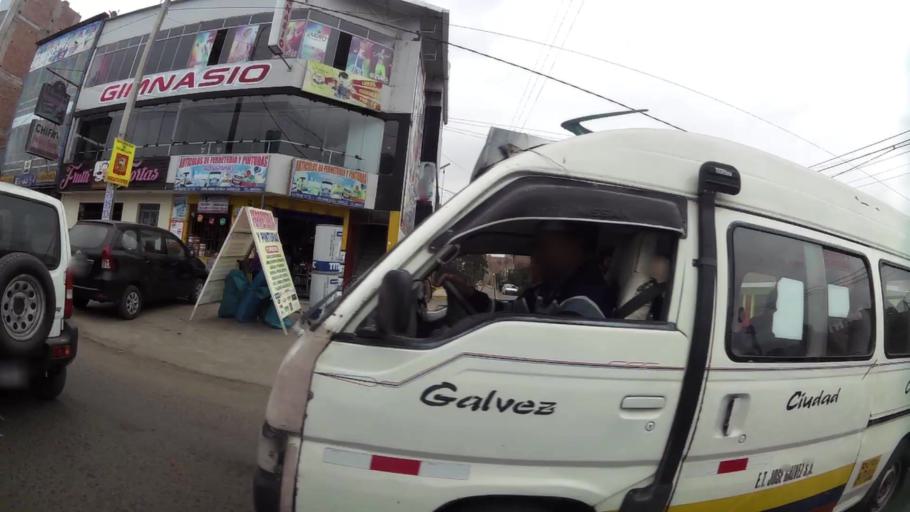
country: PE
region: Lima
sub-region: Lima
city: Surco
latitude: -12.1944
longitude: -76.9827
